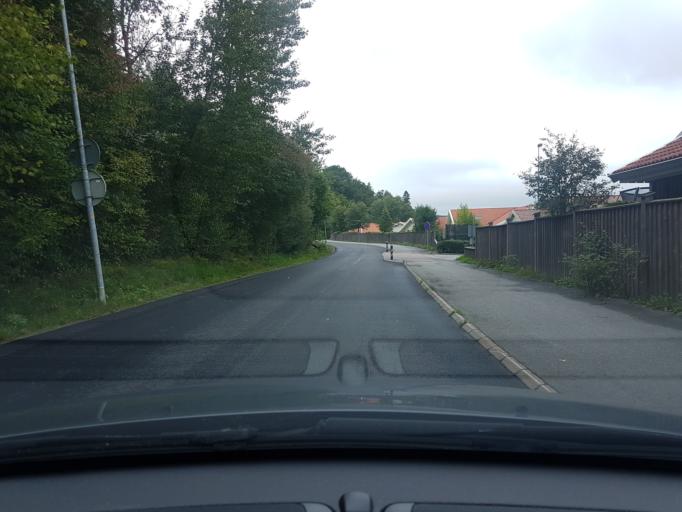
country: SE
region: Vaestra Goetaland
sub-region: Ale Kommun
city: Nodinge-Nol
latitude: 57.8853
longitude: 12.0482
